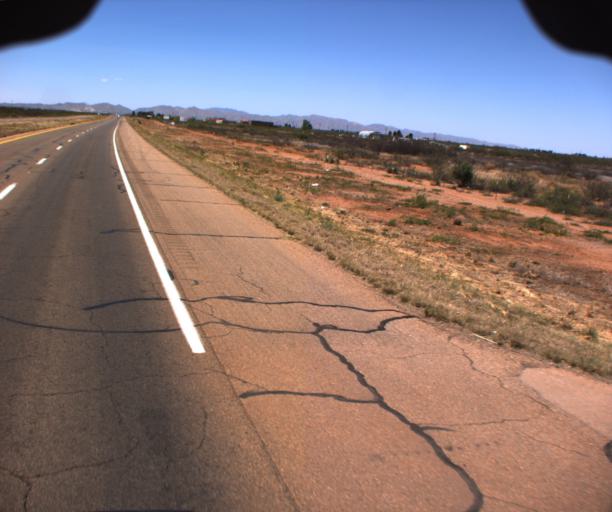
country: US
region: Arizona
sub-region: Cochise County
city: Pirtleville
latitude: 31.3545
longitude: -109.6049
